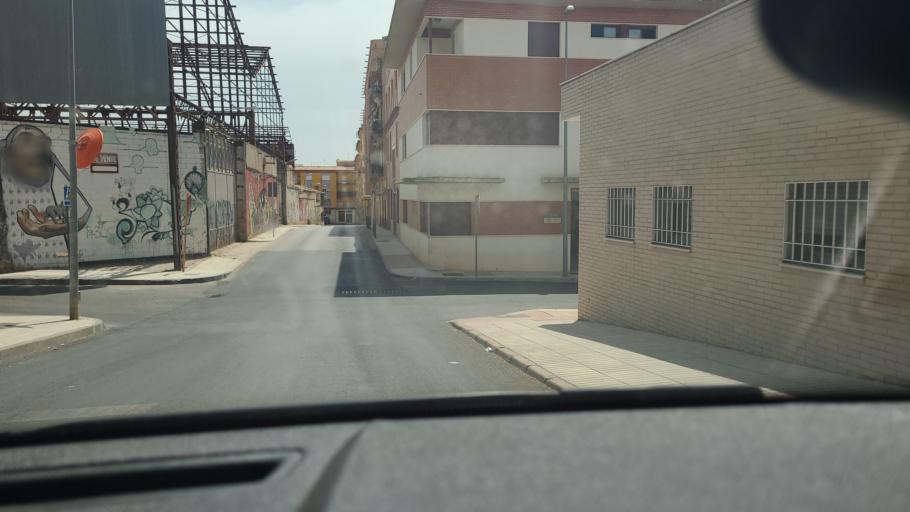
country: ES
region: Andalusia
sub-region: Provincia de Jaen
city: Linares
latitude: 38.0964
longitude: -3.6277
